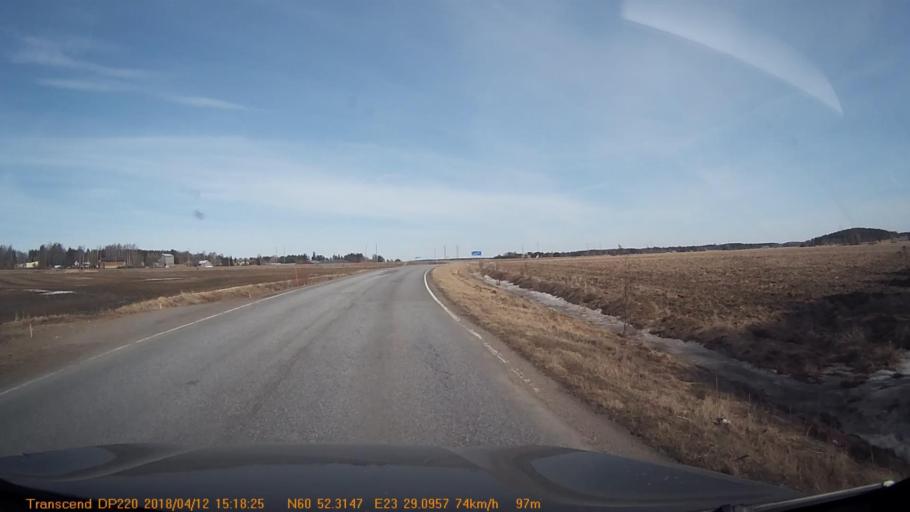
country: FI
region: Haeme
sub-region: Forssa
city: Jokioinen
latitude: 60.8720
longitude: 23.4856
